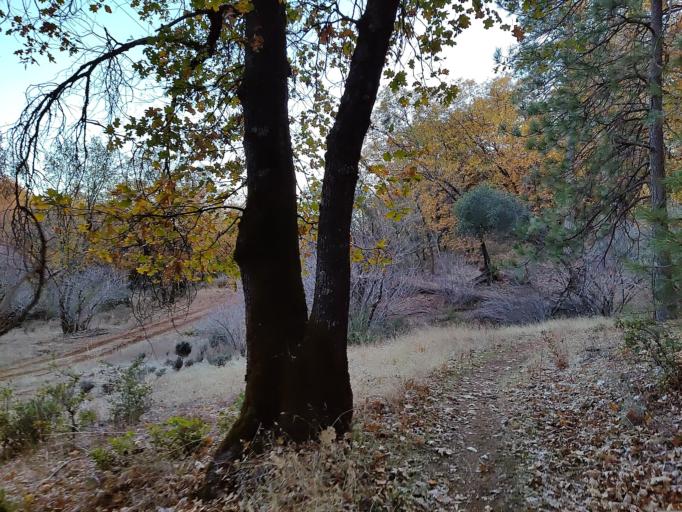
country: US
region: California
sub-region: Placer County
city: Meadow Vista
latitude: 39.0330
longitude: -120.9891
